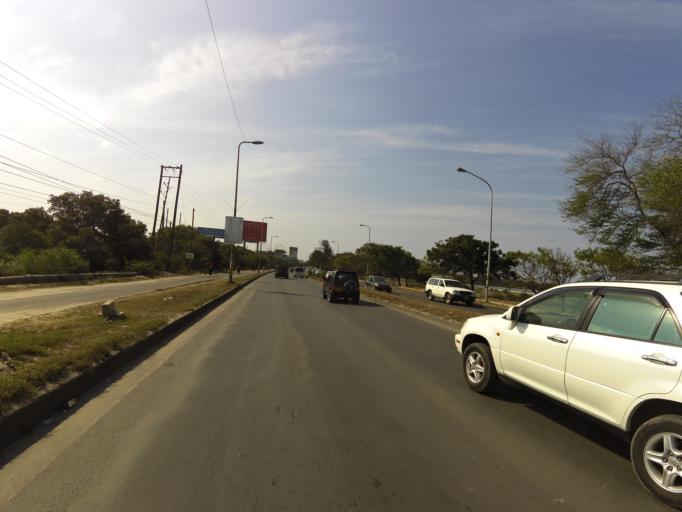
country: TZ
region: Dar es Salaam
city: Dar es Salaam
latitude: -6.7959
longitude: 39.2811
